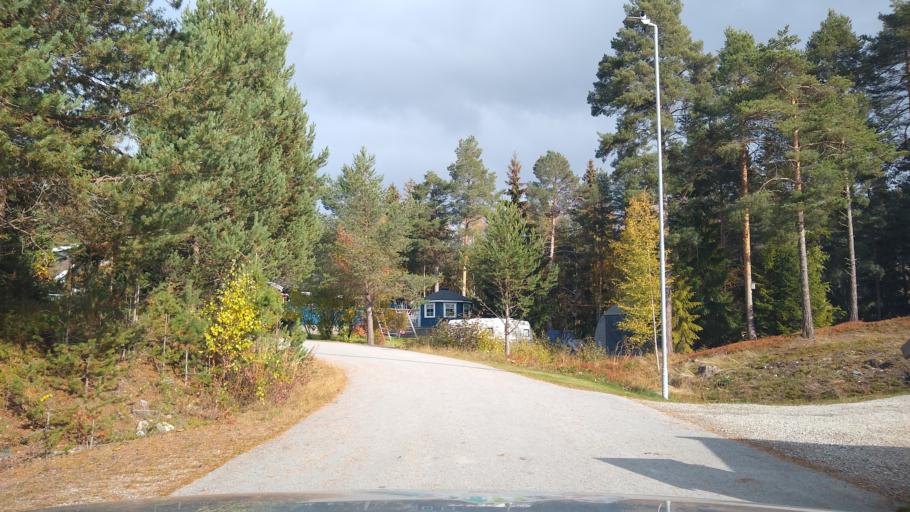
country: NO
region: Oppland
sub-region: Ringebu
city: Ringebu
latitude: 61.5398
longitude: 10.1360
